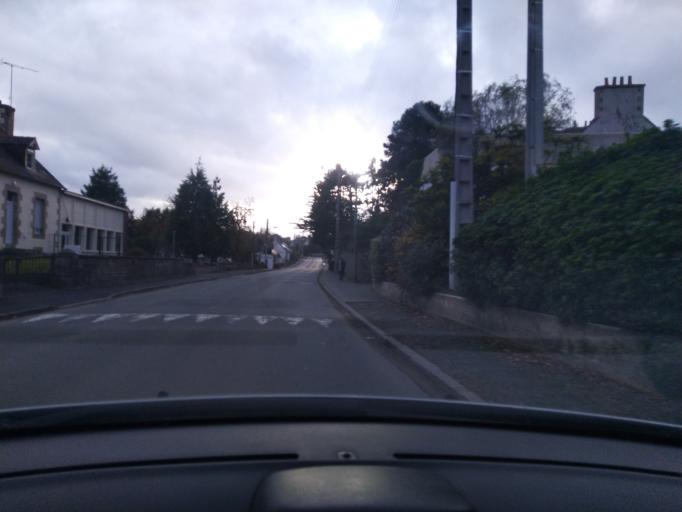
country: FR
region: Brittany
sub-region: Departement des Cotes-d'Armor
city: Plouaret
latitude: 48.6098
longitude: -3.4762
